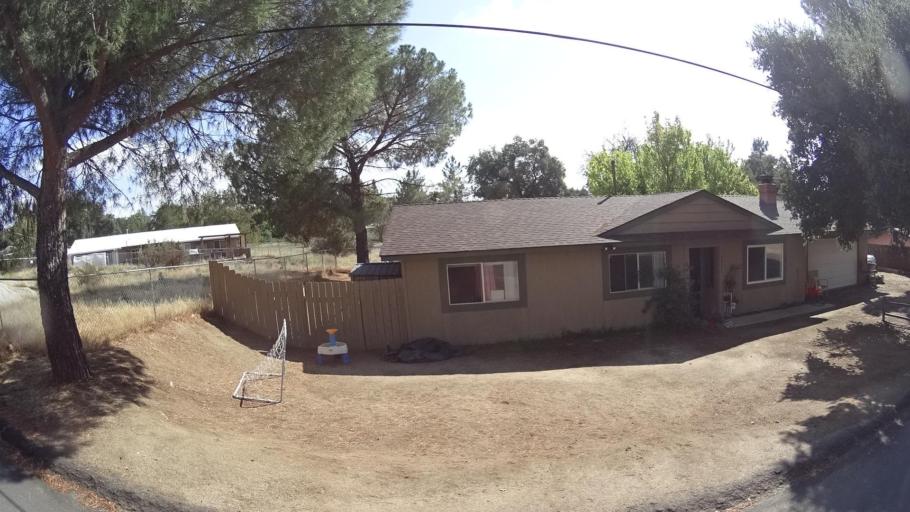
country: US
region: California
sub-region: San Diego County
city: Campo
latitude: 32.6818
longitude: -116.5037
